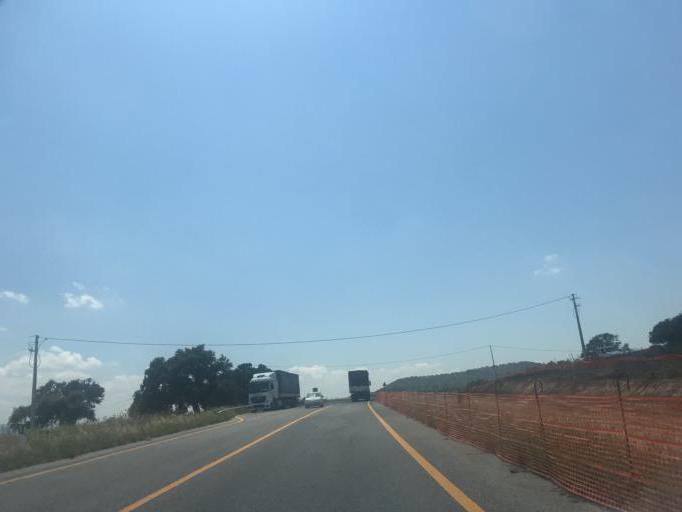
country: IT
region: Sardinia
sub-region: Provincia di Olbia-Tempio
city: Berchidda
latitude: 40.7808
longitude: 9.2456
